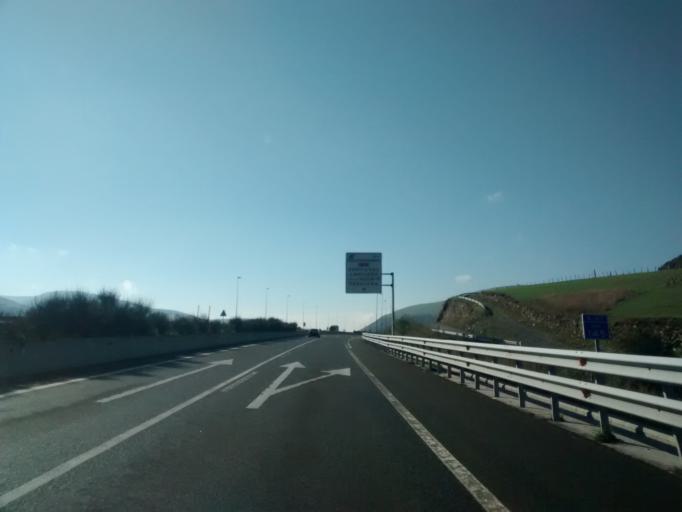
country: ES
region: Cantabria
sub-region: Provincia de Cantabria
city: Pesquera
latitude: 43.0738
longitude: -4.0859
